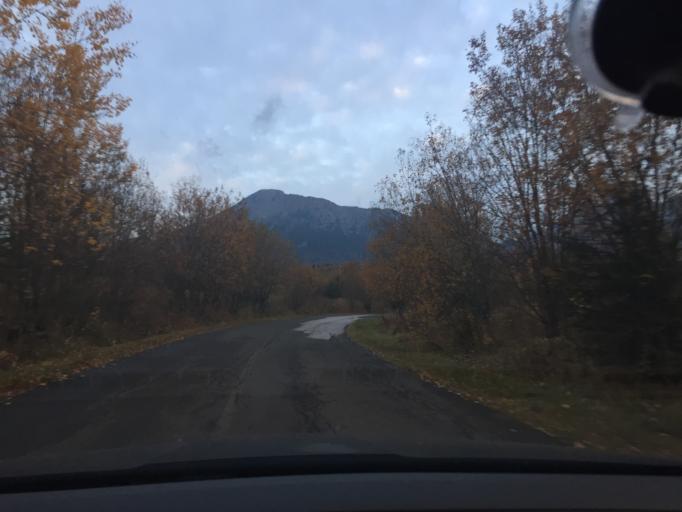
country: SK
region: Presovsky
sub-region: Okres Poprad
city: Vysoke Tatry
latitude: 49.1352
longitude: 20.2390
